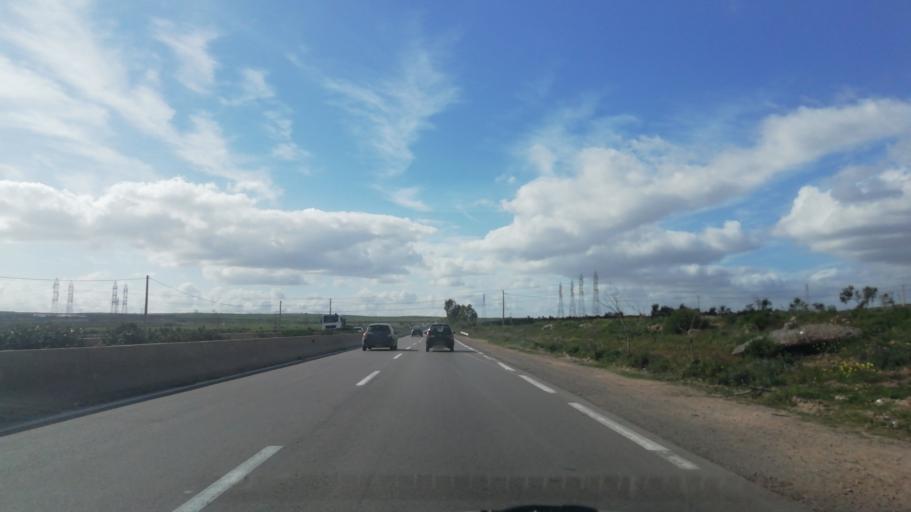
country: DZ
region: Oran
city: Ain el Bya
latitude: 35.7747
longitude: -0.1947
